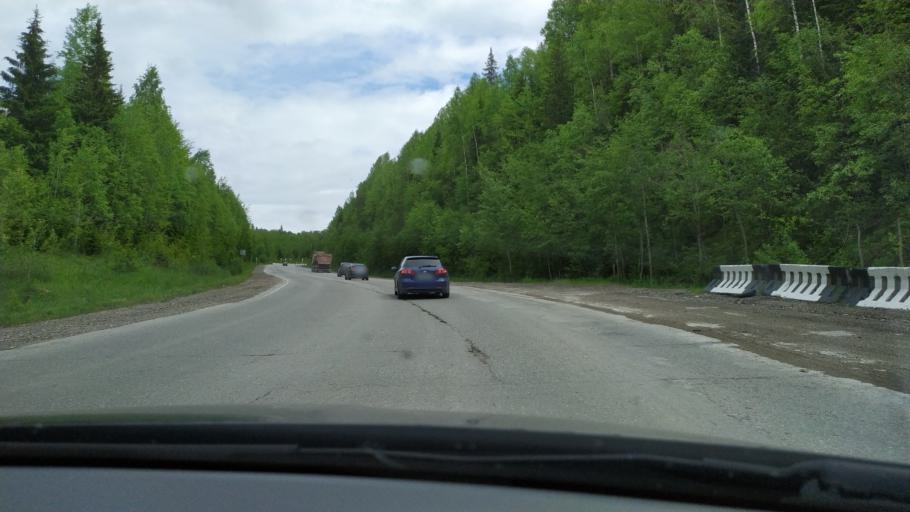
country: RU
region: Perm
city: Gremyachinsk
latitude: 58.4412
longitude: 57.8783
